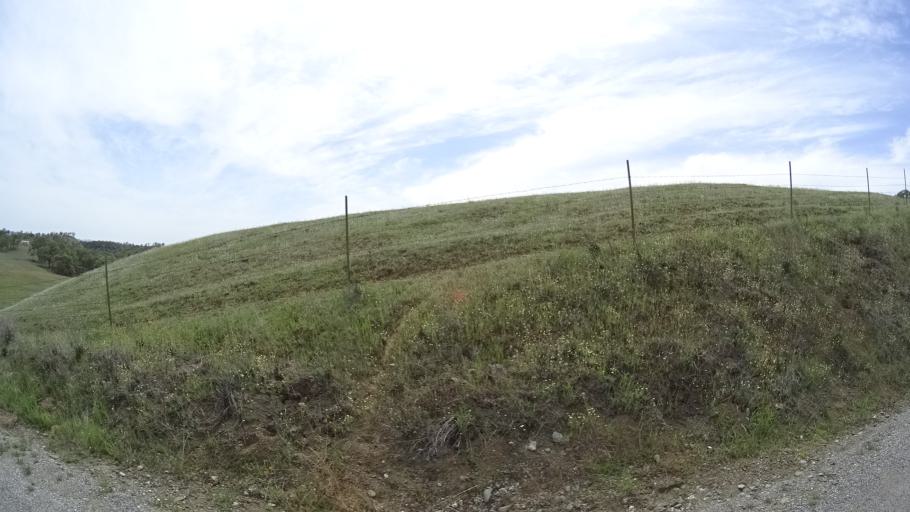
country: US
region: California
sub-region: Glenn County
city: Willows
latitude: 39.6165
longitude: -122.5892
